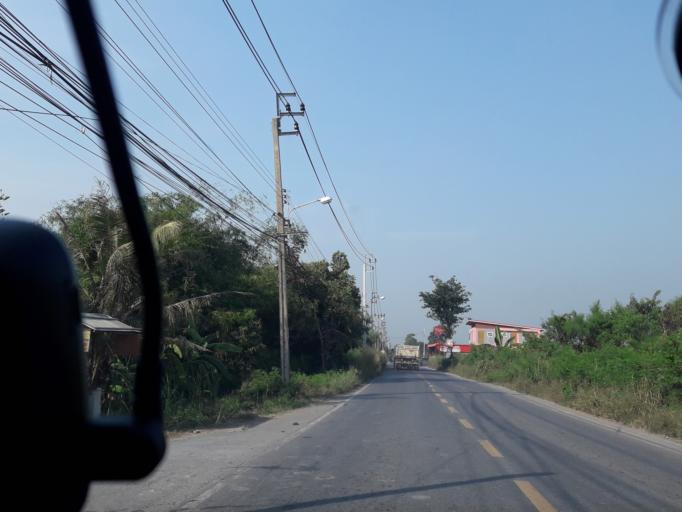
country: TH
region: Pathum Thani
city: Lam Luk Ka
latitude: 13.9097
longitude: 100.7363
